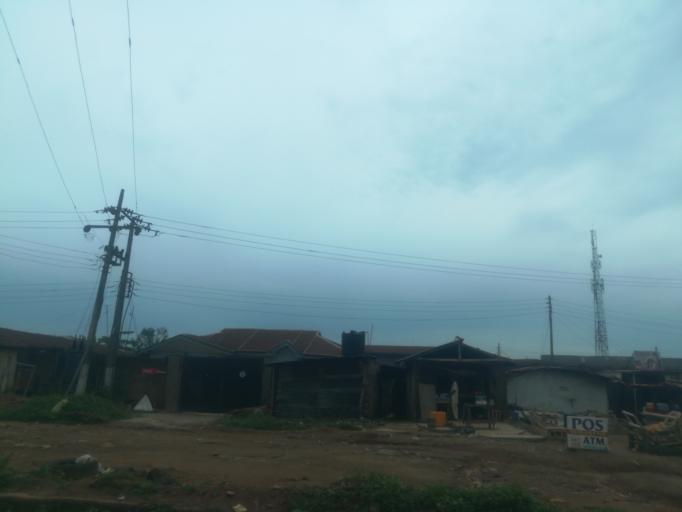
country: NG
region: Oyo
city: Ibadan
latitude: 7.3923
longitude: 3.9599
